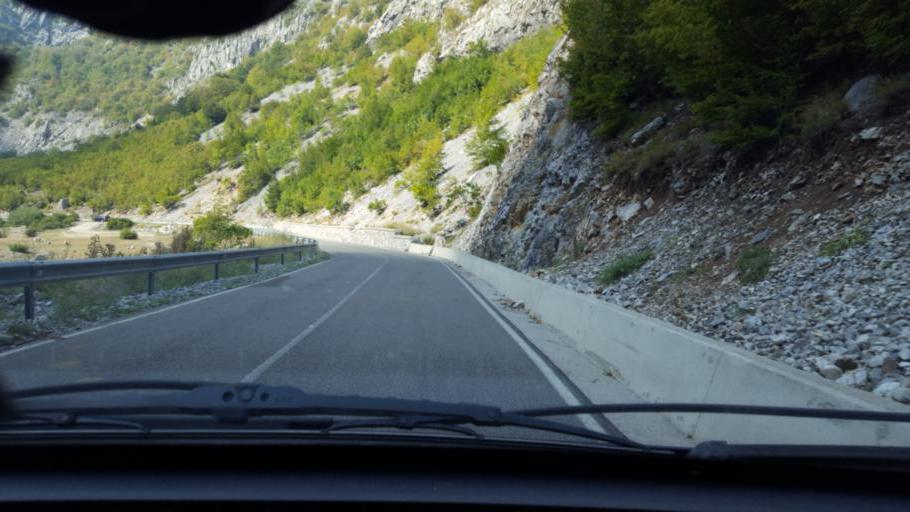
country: AL
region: Shkoder
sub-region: Rrethi i Malesia e Madhe
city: Kastrat
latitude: 42.5321
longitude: 19.6517
